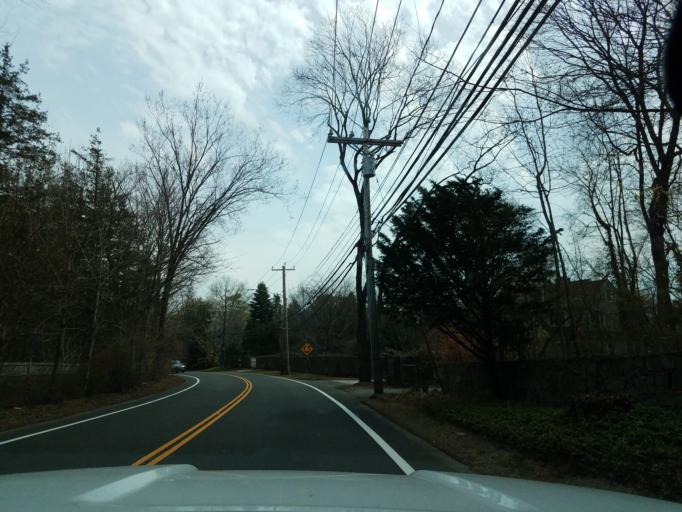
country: US
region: Connecticut
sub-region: Fairfield County
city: Greenwich
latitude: 41.0319
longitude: -73.6348
